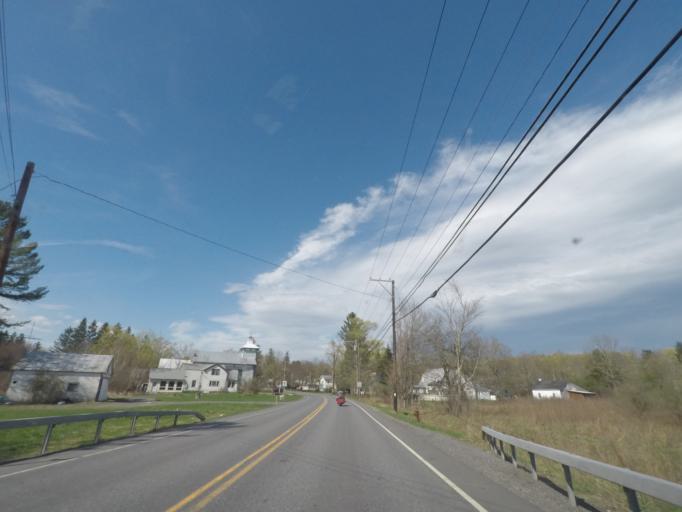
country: US
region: New York
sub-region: Greene County
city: Cairo
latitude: 42.4115
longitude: -74.0225
